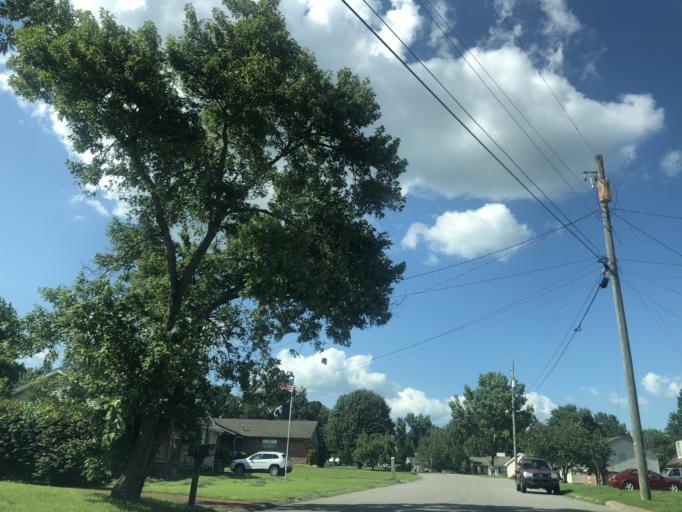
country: US
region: Tennessee
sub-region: Wilson County
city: Green Hill
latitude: 36.1984
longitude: -86.5997
